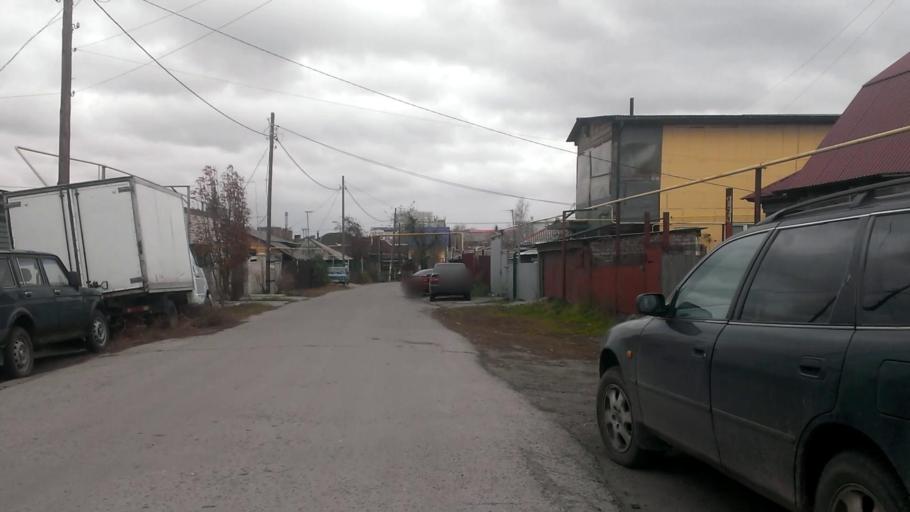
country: RU
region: Altai Krai
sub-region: Gorod Barnaulskiy
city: Barnaul
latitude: 53.3521
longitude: 83.7457
